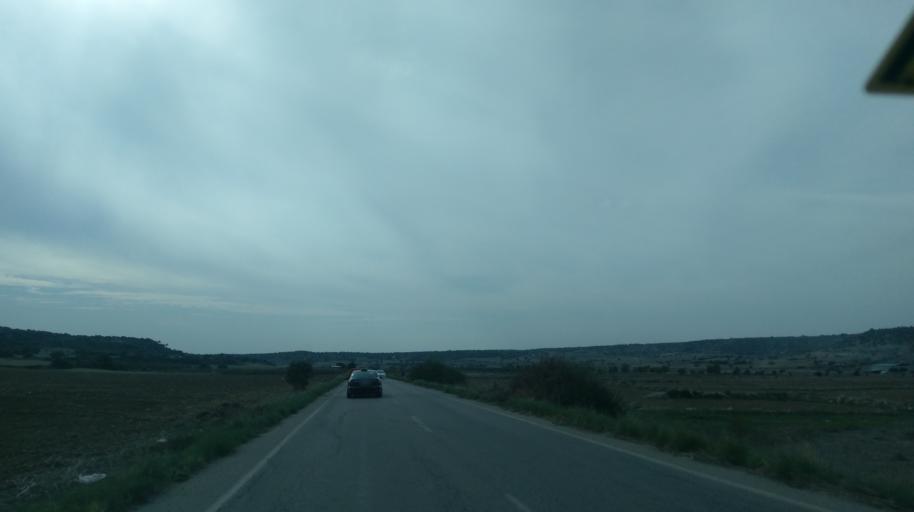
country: CY
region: Ammochostos
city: Leonarisso
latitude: 35.4616
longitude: 34.1358
